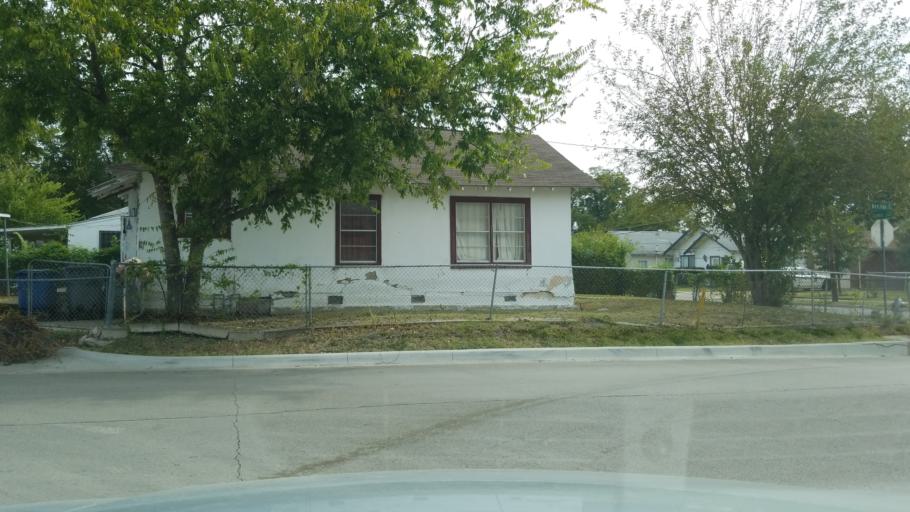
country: US
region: Texas
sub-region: Dallas County
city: Dallas
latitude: 32.7849
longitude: -96.7445
